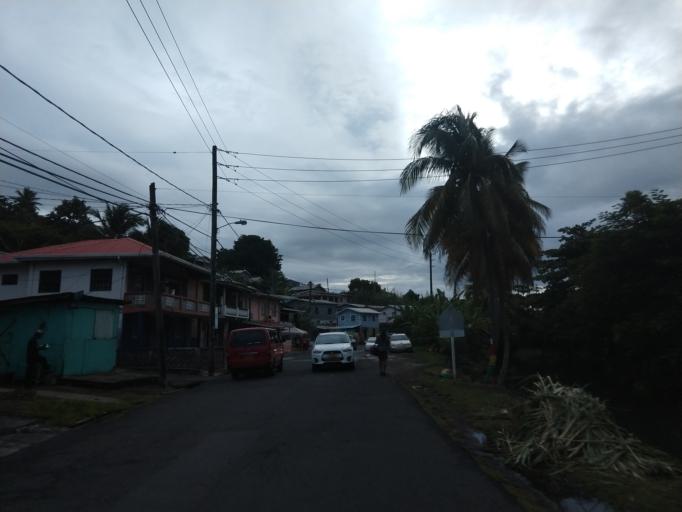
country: GD
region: Saint George
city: Saint George's
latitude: 12.0577
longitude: -61.7519
